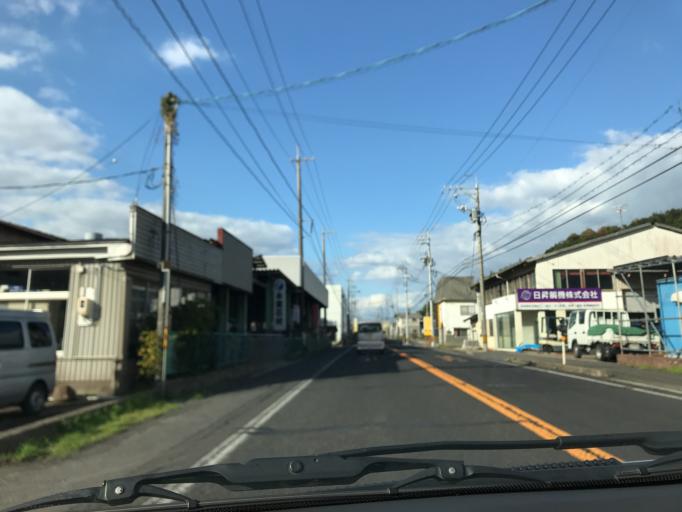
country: JP
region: Shimane
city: Yasugicho
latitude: 35.4279
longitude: 133.2719
